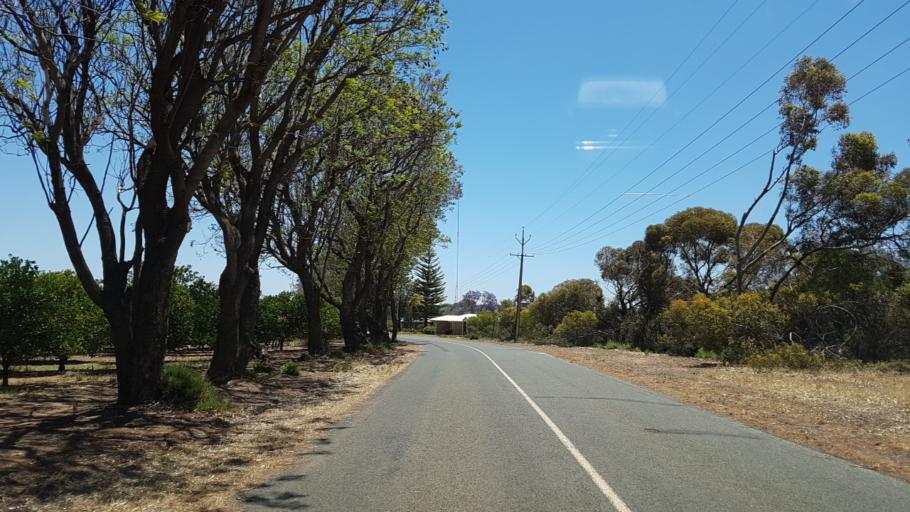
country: AU
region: South Australia
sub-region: Loxton Waikerie
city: Waikerie
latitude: -34.1675
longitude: 140.0365
